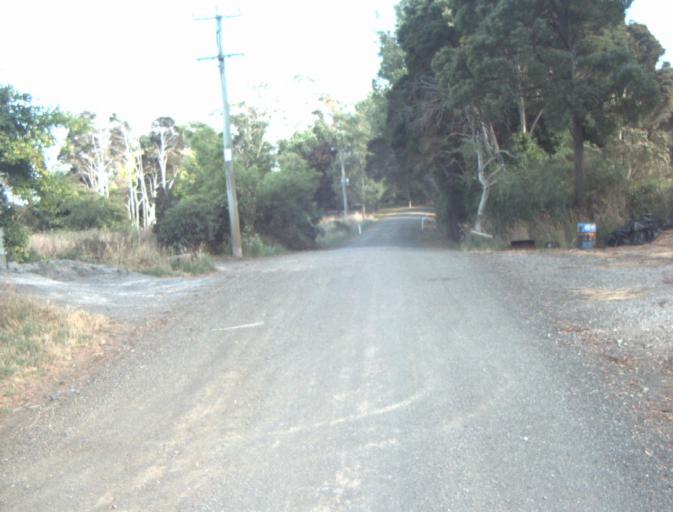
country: AU
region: Tasmania
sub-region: Launceston
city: Mayfield
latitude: -41.2738
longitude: 147.1841
